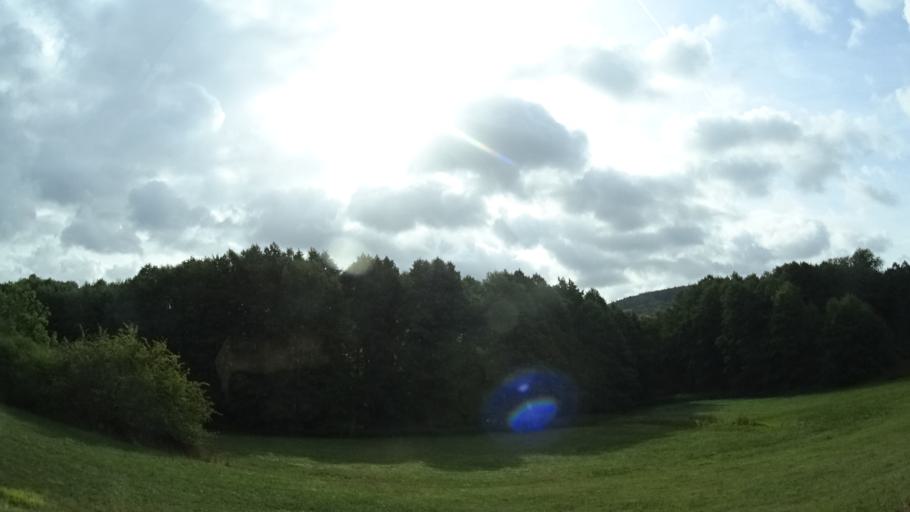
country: DE
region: Thuringia
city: Unterkatz
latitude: 50.6126
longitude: 10.2377
